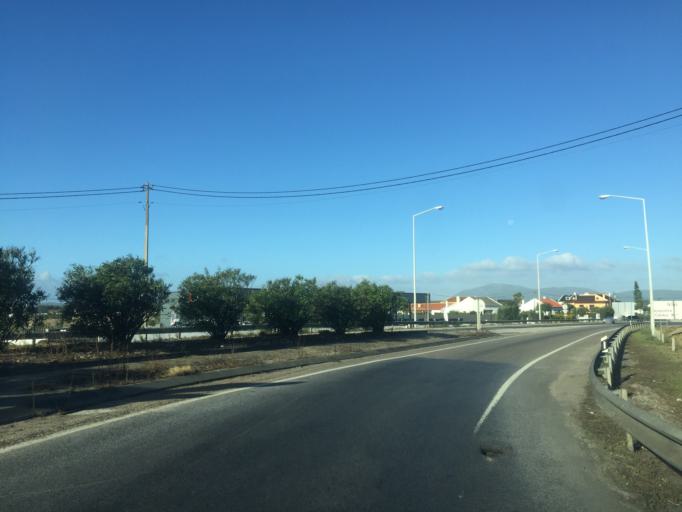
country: PT
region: Lisbon
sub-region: Azambuja
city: Aveiras de Cima
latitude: 39.1454
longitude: -8.9023
